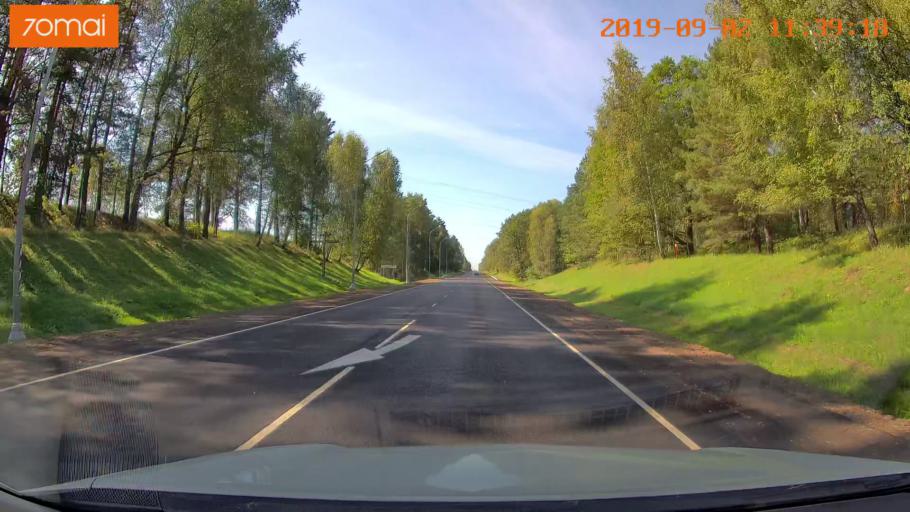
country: RU
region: Smolensk
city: Oster
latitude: 53.9087
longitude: 32.7256
